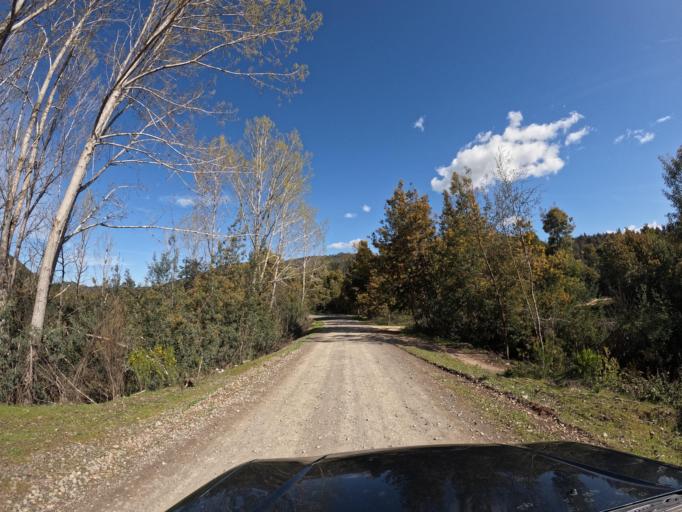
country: CL
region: Biobio
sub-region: Provincia de Concepcion
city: Chiguayante
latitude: -37.0673
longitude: -72.8798
